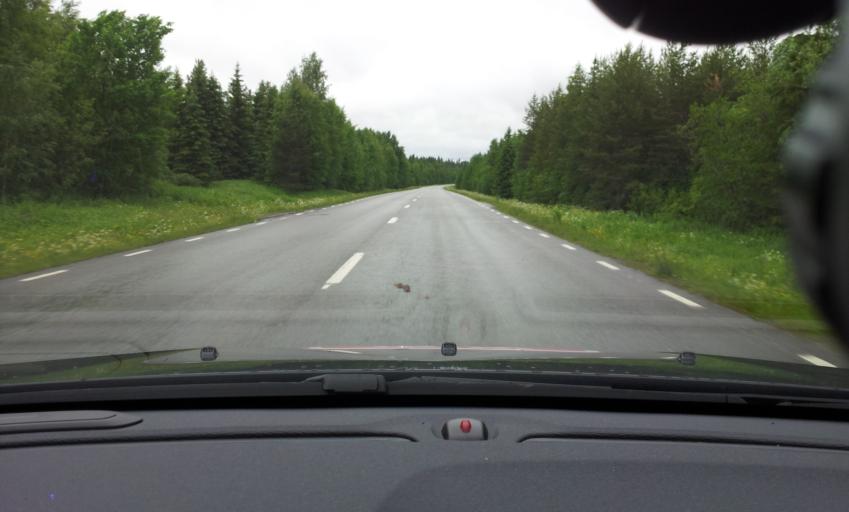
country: SE
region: Jaemtland
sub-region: Krokoms Kommun
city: Krokom
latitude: 63.3708
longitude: 14.5074
